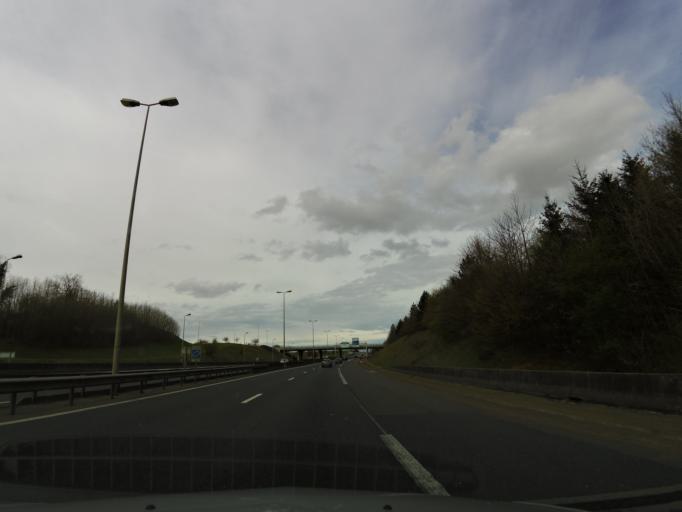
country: FR
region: Lower Normandy
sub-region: Departement du Calvados
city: Bretteville-sur-Odon
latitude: 49.1603
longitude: -0.4272
